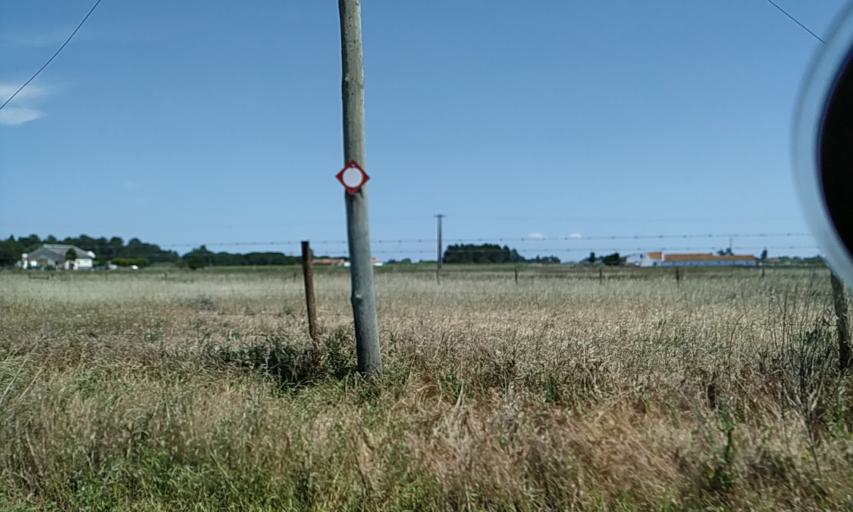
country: PT
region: Setubal
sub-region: Palmela
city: Pinhal Novo
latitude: 38.6501
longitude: -8.7436
